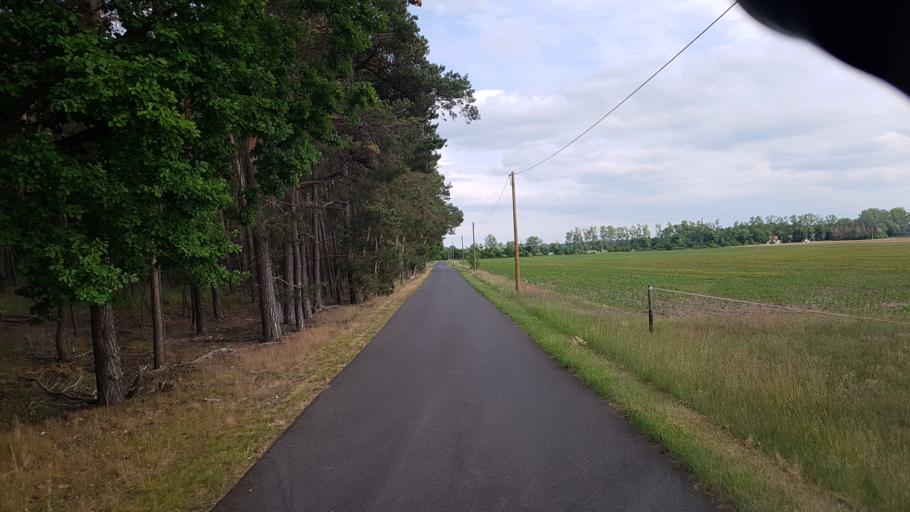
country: DE
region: Brandenburg
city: Herzberg
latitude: 51.7227
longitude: 13.2768
